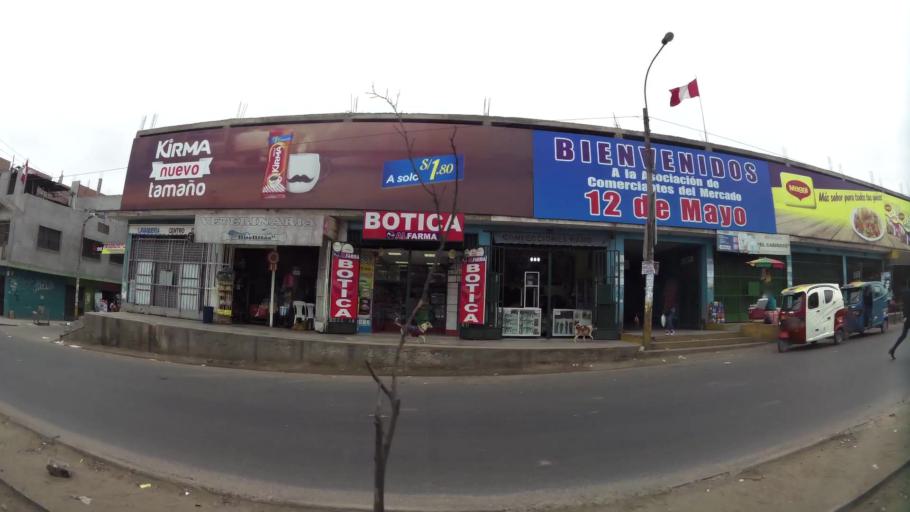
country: PE
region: Lima
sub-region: Lima
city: Surco
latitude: -12.1919
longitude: -76.9562
